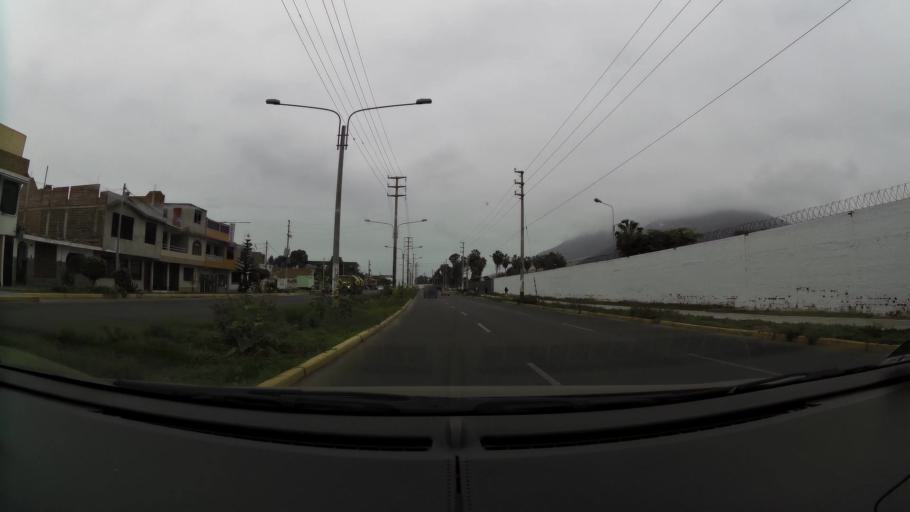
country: PE
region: Ancash
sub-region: Provincia de Santa
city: Chimbote
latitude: -9.0655
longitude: -78.5958
